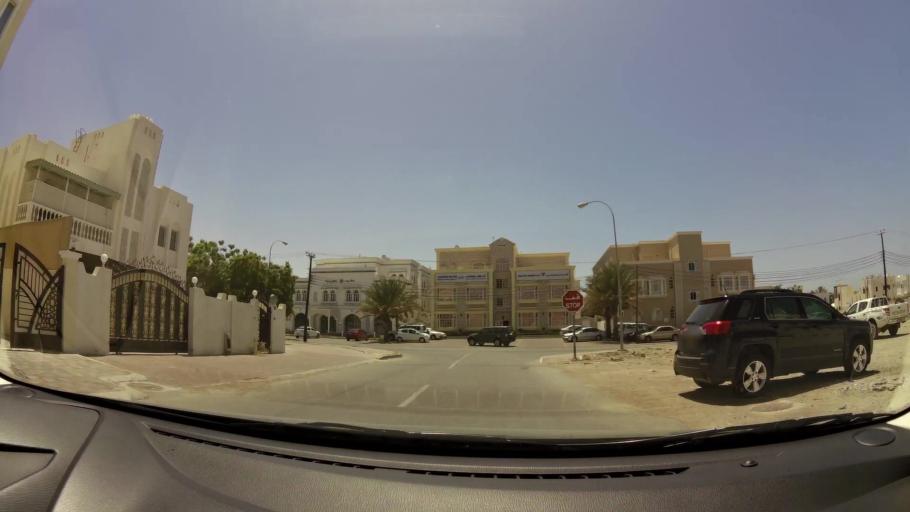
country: OM
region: Muhafazat Masqat
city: Bawshar
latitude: 23.5926
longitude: 58.3782
